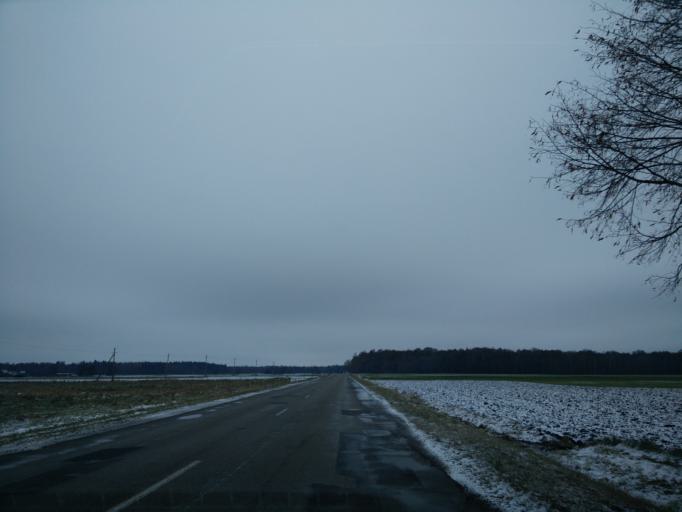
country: LT
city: Ariogala
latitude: 55.3937
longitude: 23.3408
